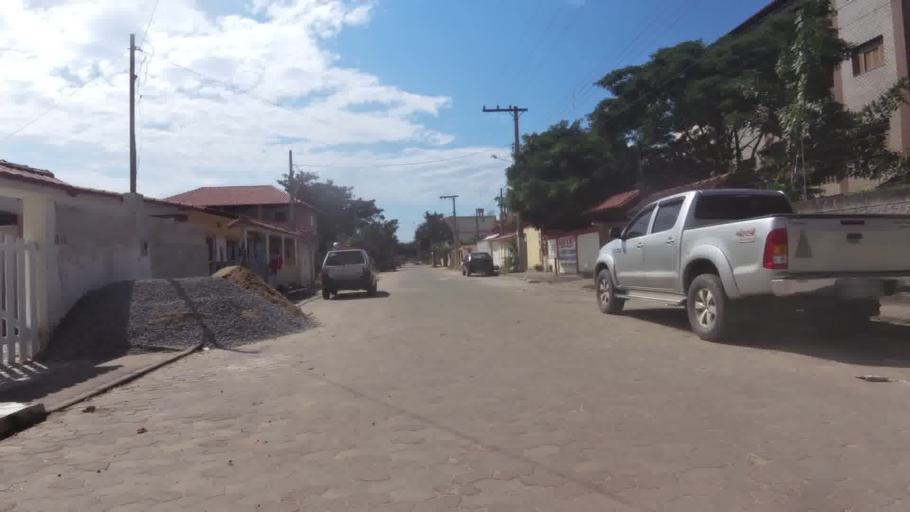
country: BR
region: Espirito Santo
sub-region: Piuma
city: Piuma
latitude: -20.8444
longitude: -40.7434
